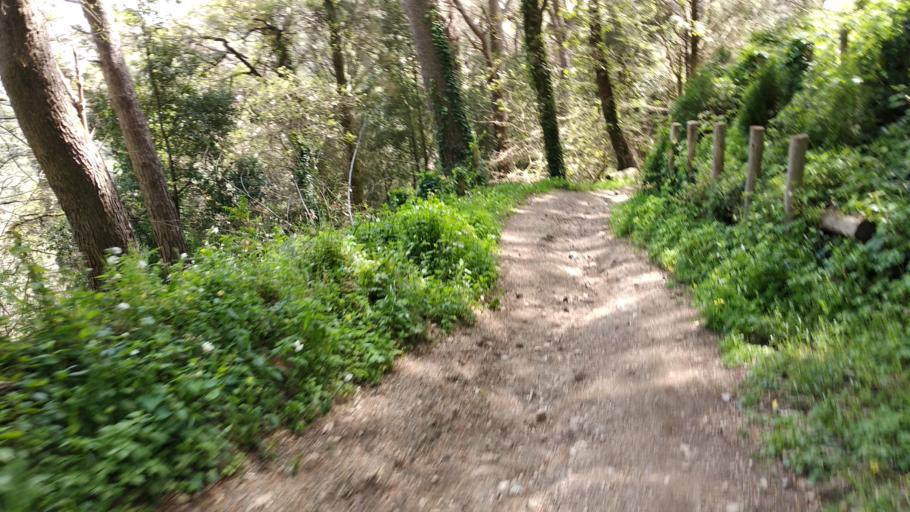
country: IT
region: Sicily
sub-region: Messina
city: Castanea delle Furie
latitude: 38.2143
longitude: 15.5072
